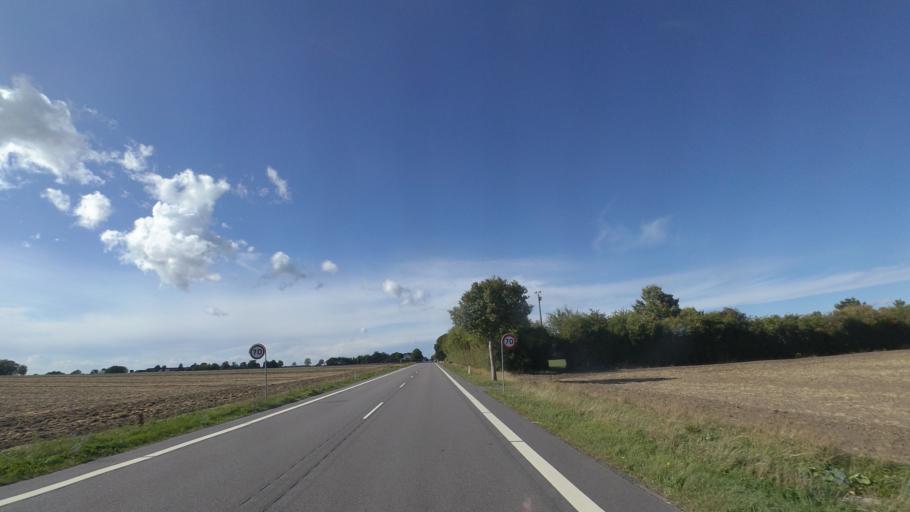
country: DK
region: Capital Region
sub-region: Bornholm Kommune
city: Akirkeby
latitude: 55.0701
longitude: 14.8158
